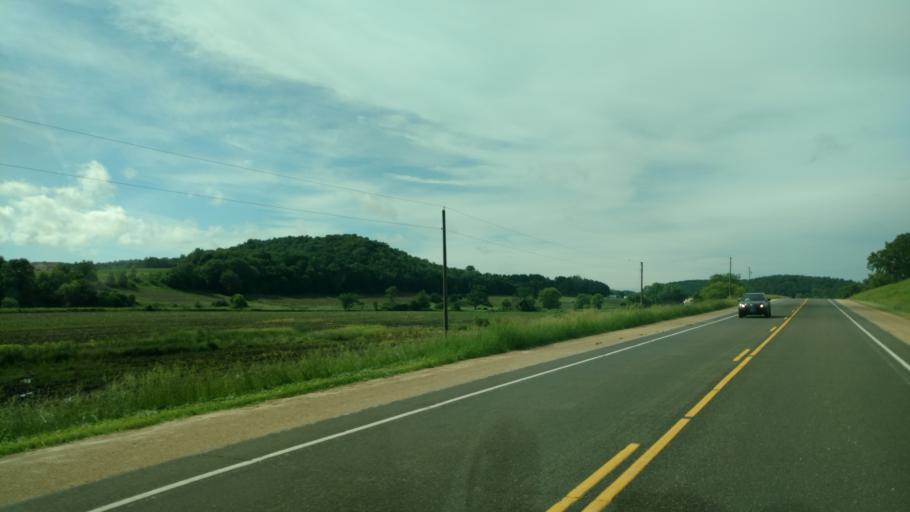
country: US
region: Wisconsin
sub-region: Monroe County
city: Tomah
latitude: 43.8569
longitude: -90.4737
